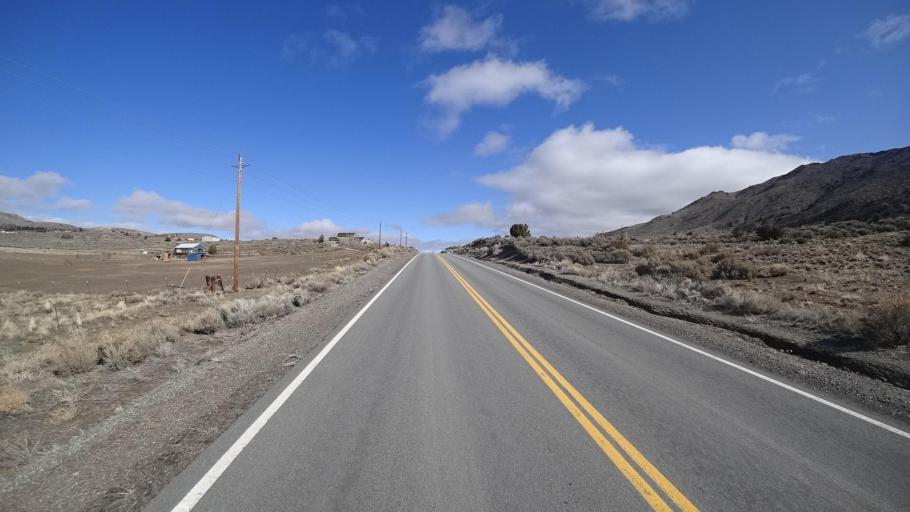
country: US
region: Nevada
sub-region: Washoe County
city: Cold Springs
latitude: 39.7576
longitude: -119.8857
